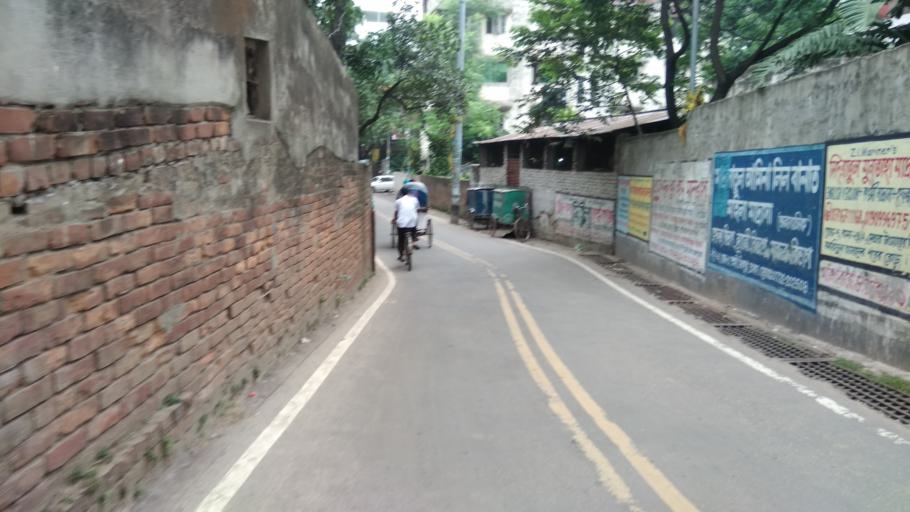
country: BD
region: Dhaka
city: Tungi
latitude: 23.8218
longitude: 90.3614
